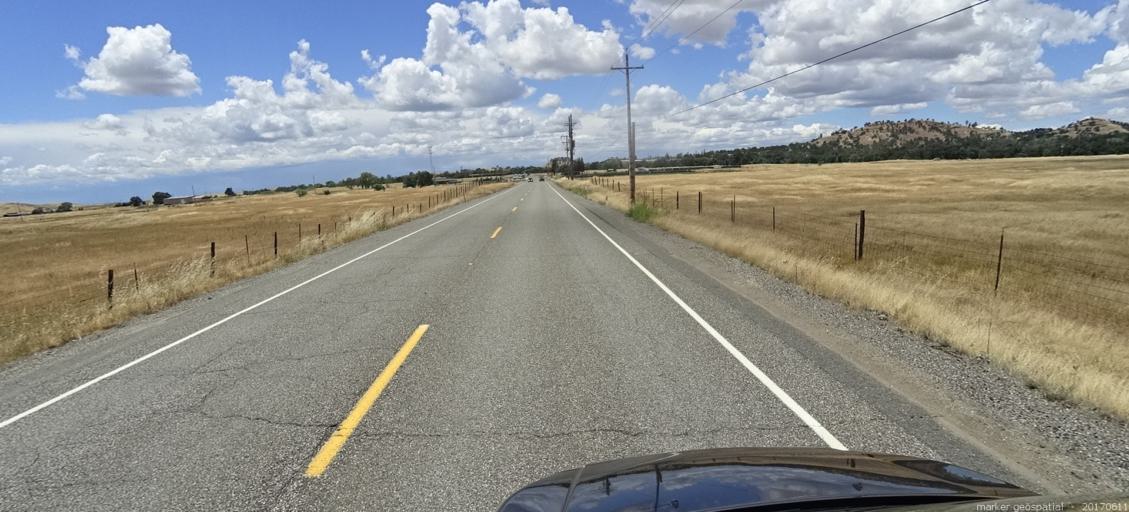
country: US
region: California
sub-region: Butte County
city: Paradise
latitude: 39.6474
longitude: -121.6289
